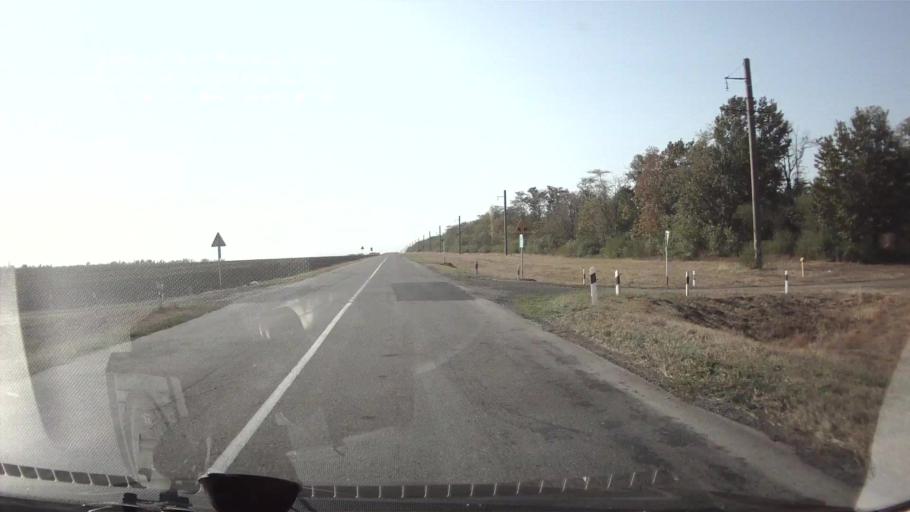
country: RU
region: Rostov
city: Tselina
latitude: 46.5189
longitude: 40.8996
